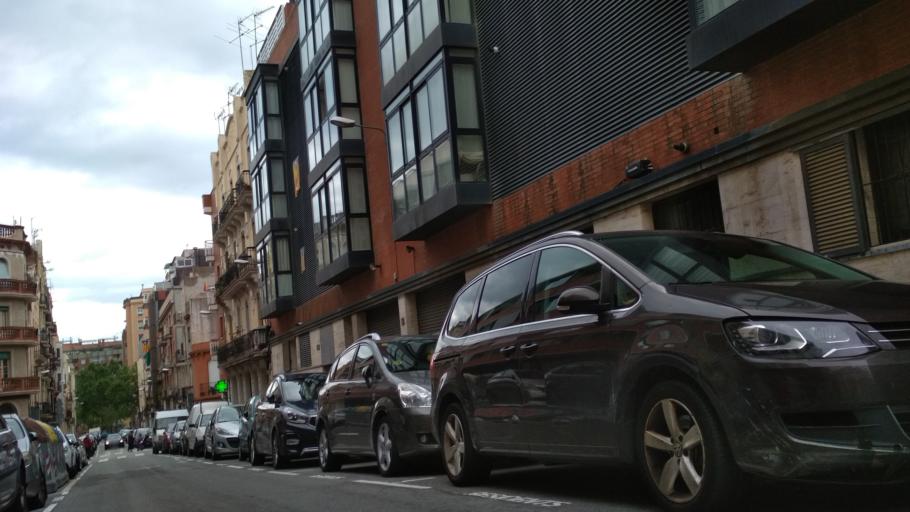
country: ES
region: Catalonia
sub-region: Provincia de Barcelona
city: Sant Marti
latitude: 41.4124
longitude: 2.1838
